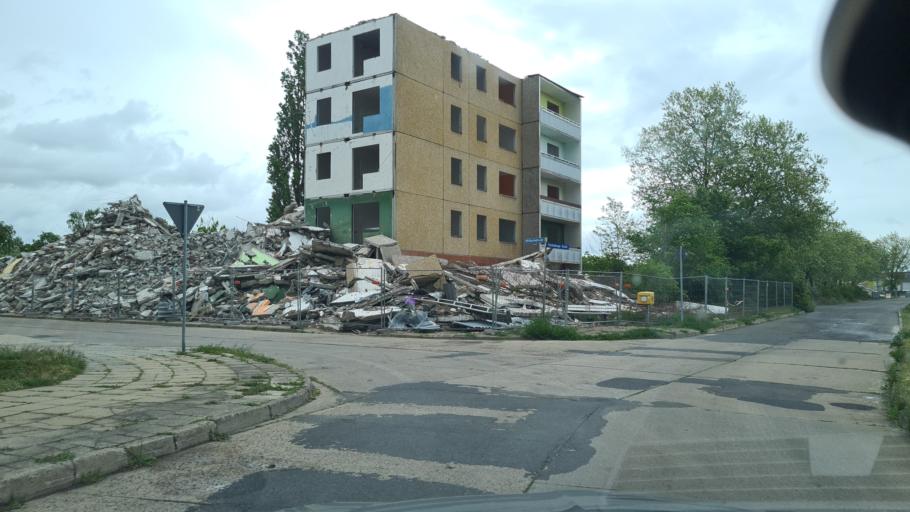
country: DE
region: Brandenburg
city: Eisenhuettenstadt
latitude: 52.1425
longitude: 14.6600
